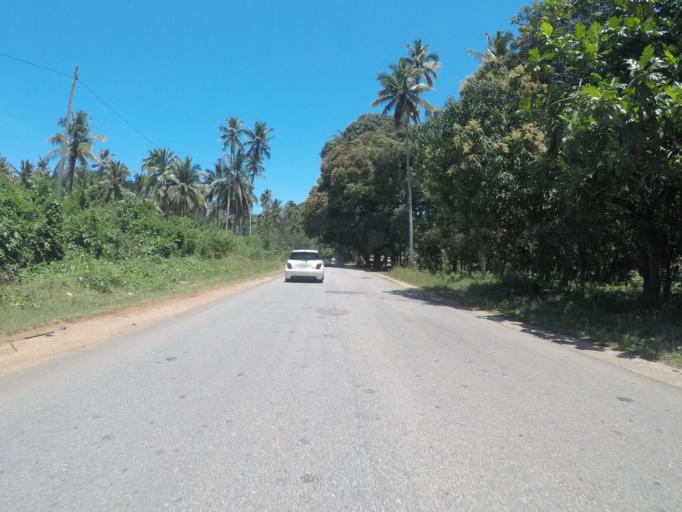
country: TZ
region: Zanzibar Central/South
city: Koani
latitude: -6.2109
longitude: 39.3241
